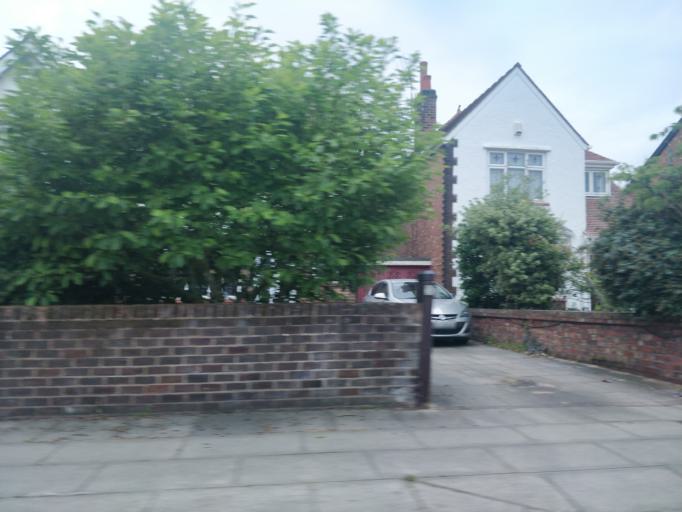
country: GB
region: England
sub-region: Sefton
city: Southport
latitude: 53.6584
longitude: -2.9686
